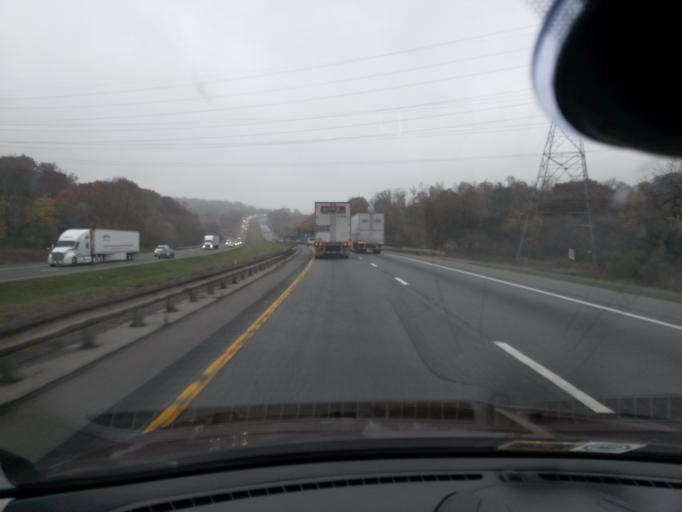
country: US
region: Virginia
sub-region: Montgomery County
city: Shawsville
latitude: 37.2515
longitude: -80.1829
